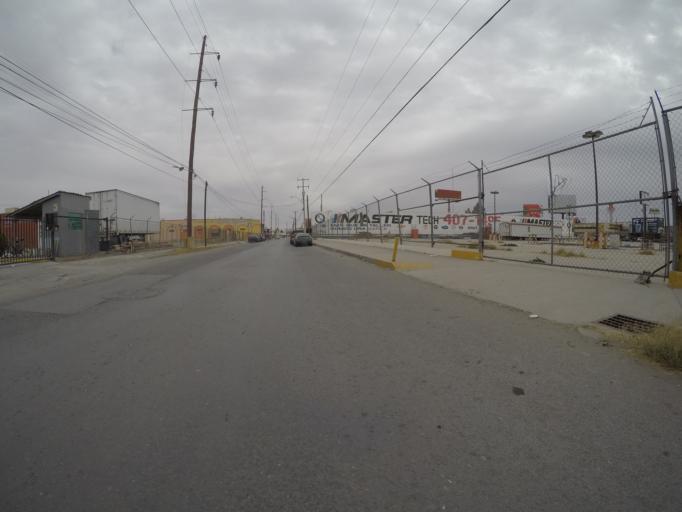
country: MX
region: Chihuahua
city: Ciudad Juarez
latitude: 31.7402
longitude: -106.4280
